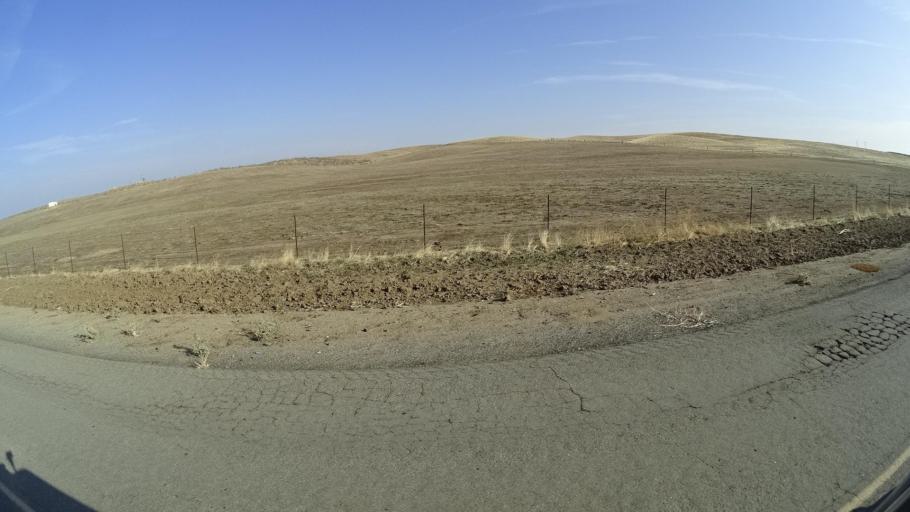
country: US
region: California
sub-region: Tulare County
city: Richgrove
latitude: 35.6468
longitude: -119.0570
